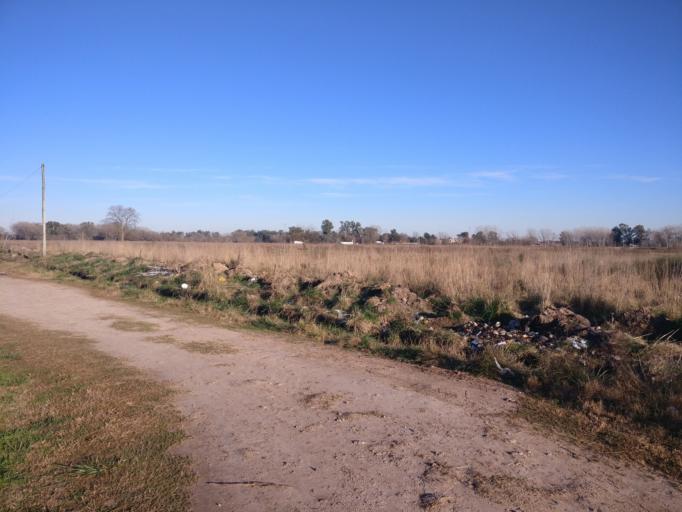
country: AR
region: Buenos Aires
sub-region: Partido de Ezeiza
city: Ezeiza
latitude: -34.9352
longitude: -58.6050
